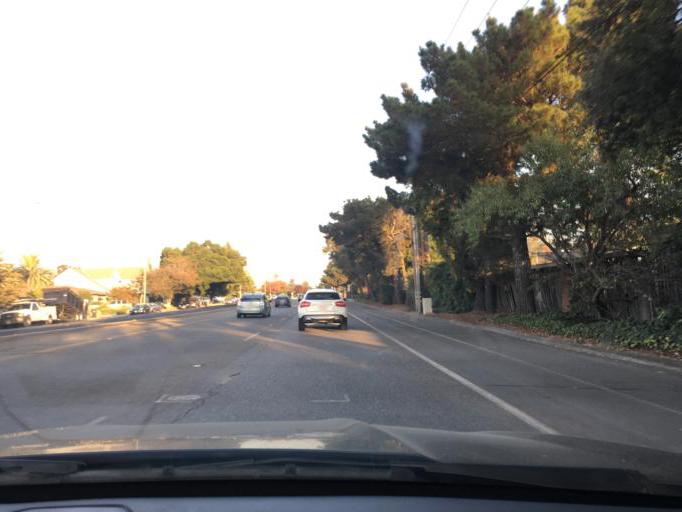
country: US
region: California
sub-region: Santa Clara County
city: Saratoga
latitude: 37.2934
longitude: -122.0134
